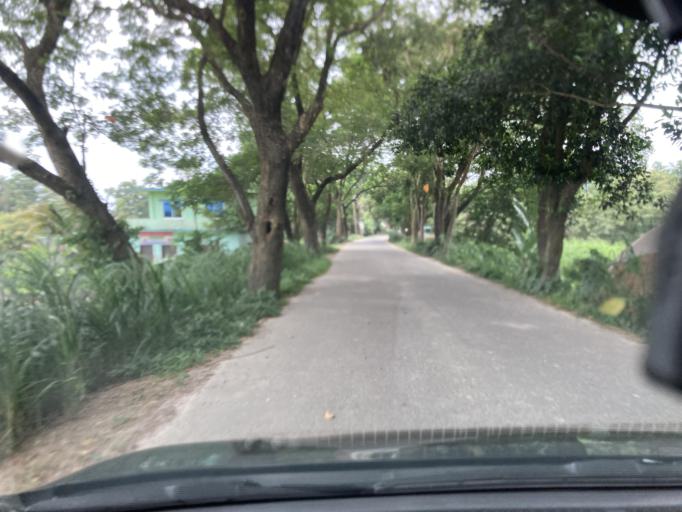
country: BD
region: Dhaka
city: Dohar
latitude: 23.8020
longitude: 90.0468
